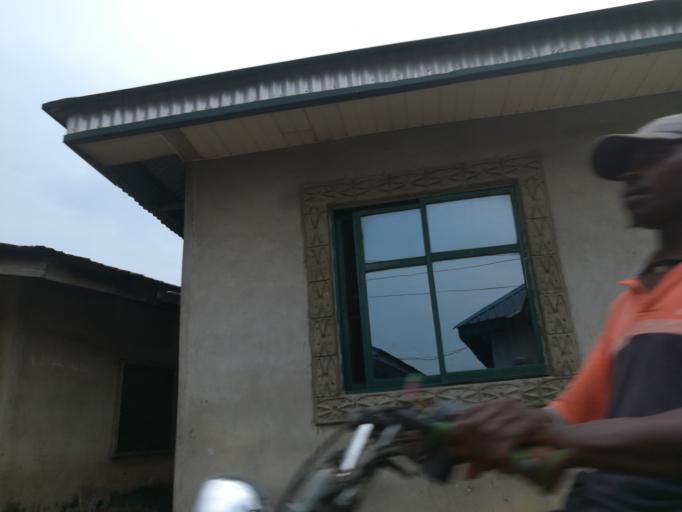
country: NG
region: Rivers
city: Okrika
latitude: 4.7891
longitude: 7.1272
